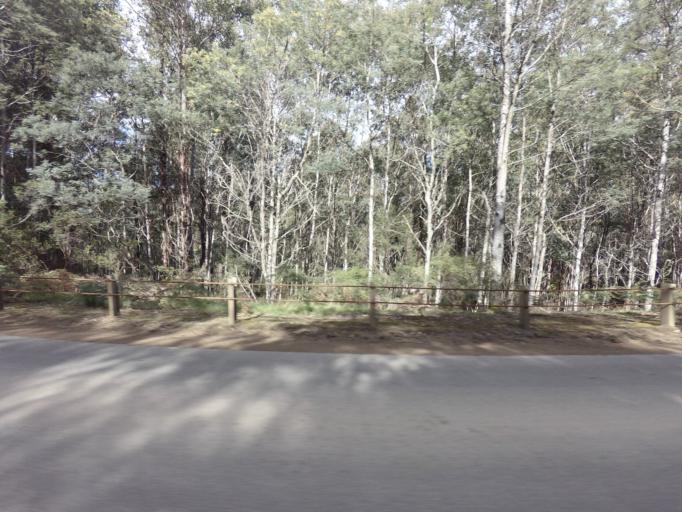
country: AU
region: Tasmania
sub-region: Huon Valley
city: Geeveston
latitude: -43.3435
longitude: 146.9626
